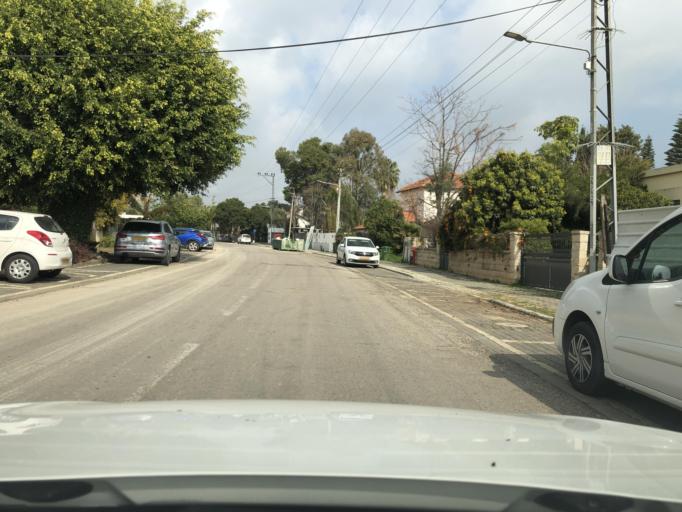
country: IL
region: Central District
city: Yehud
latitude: 32.0375
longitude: 34.8976
